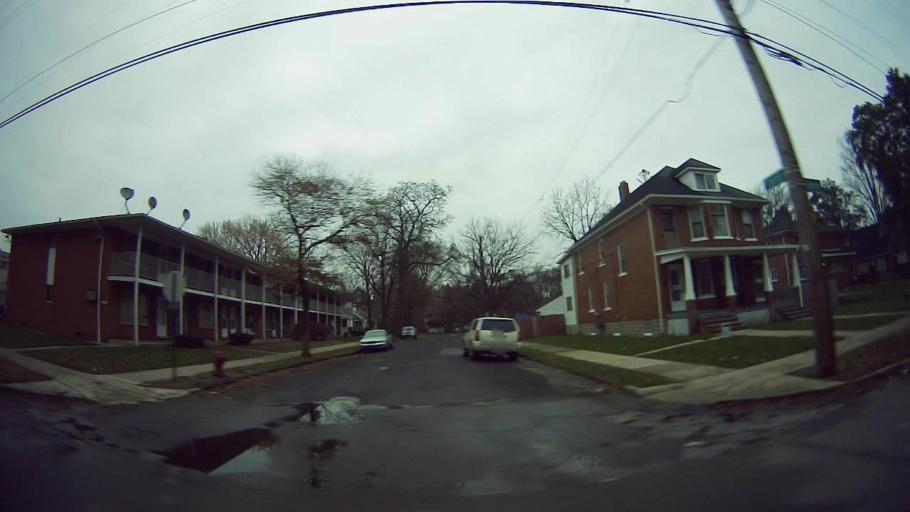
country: US
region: Michigan
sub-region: Wayne County
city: Redford
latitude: 42.4224
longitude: -83.2581
